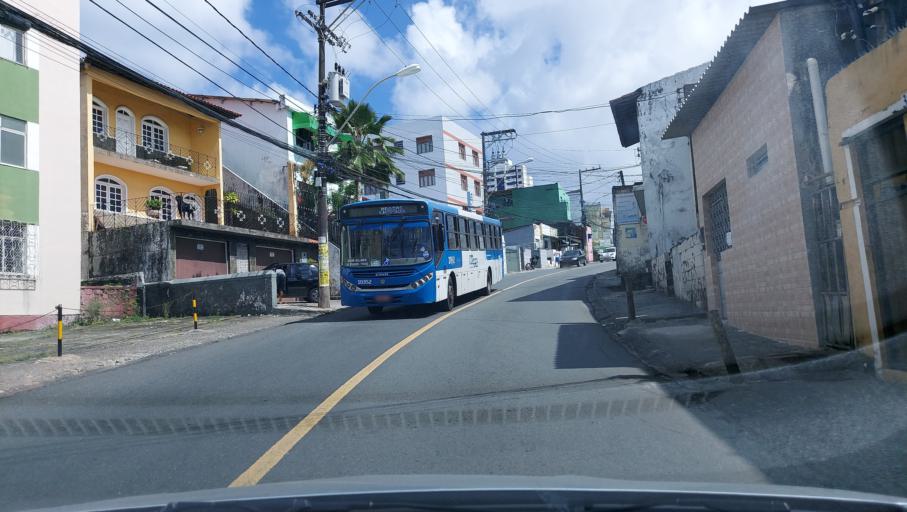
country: BR
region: Bahia
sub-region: Salvador
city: Salvador
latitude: -12.9897
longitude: -38.4786
